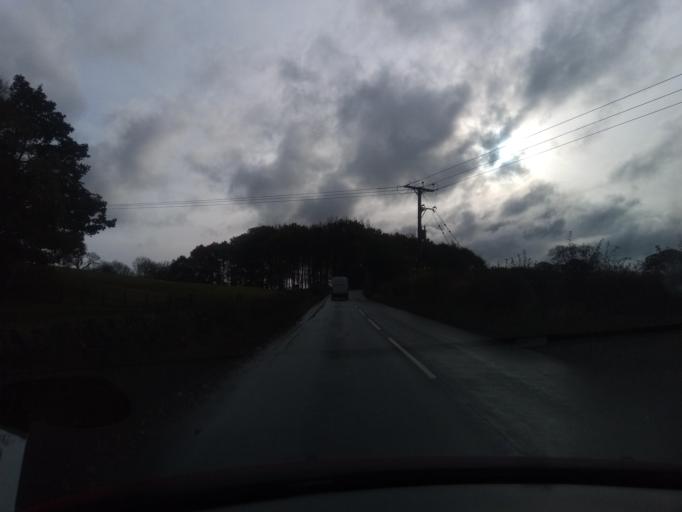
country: GB
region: England
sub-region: Northumberland
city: Birtley
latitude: 55.0585
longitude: -2.1925
